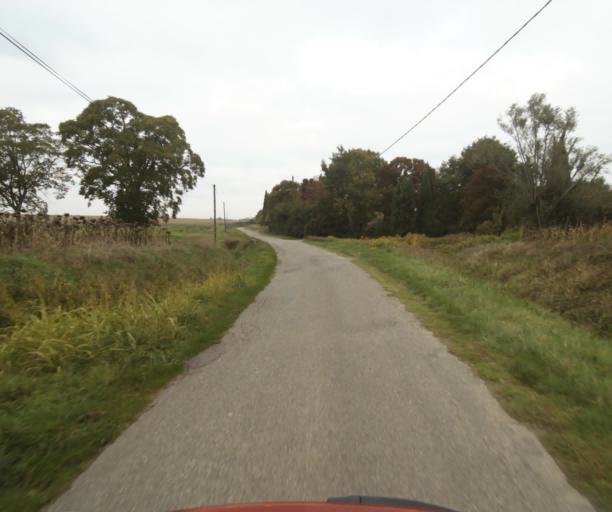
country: FR
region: Midi-Pyrenees
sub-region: Departement du Tarn-et-Garonne
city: Verdun-sur-Garonne
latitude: 43.8082
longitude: 1.2127
